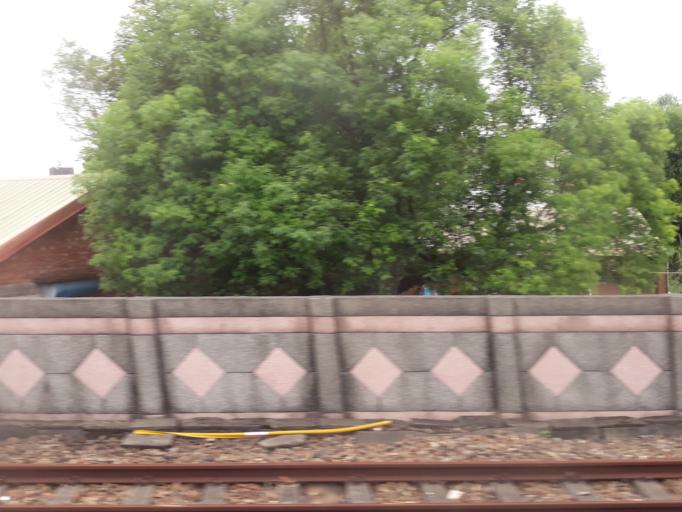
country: TW
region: Taiwan
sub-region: Yilan
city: Yilan
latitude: 24.7017
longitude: 121.7752
